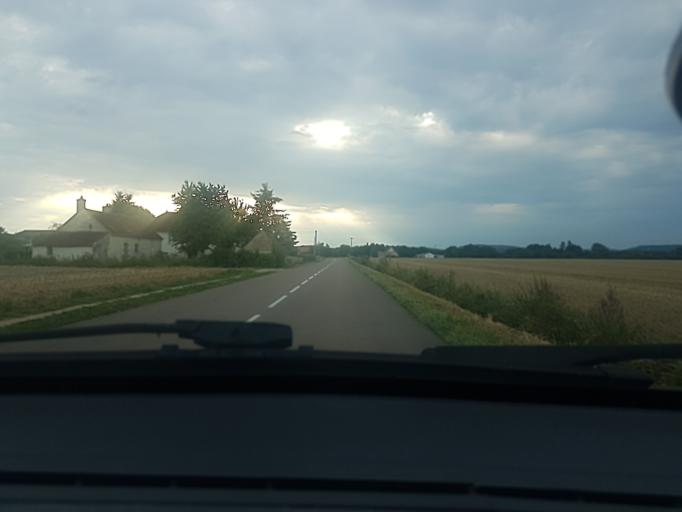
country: FR
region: Bourgogne
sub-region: Departement de Saone-et-Loire
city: Buxy
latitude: 46.7277
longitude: 4.7550
